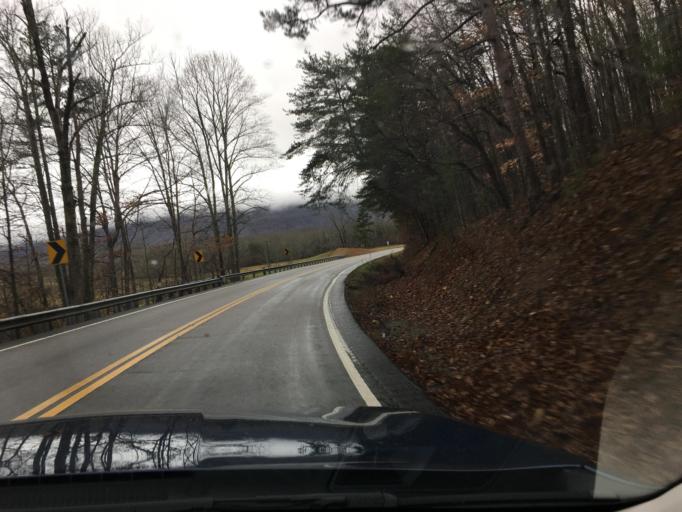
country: US
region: Tennessee
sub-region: Rhea County
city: Spring City
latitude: 35.8277
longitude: -84.9086
